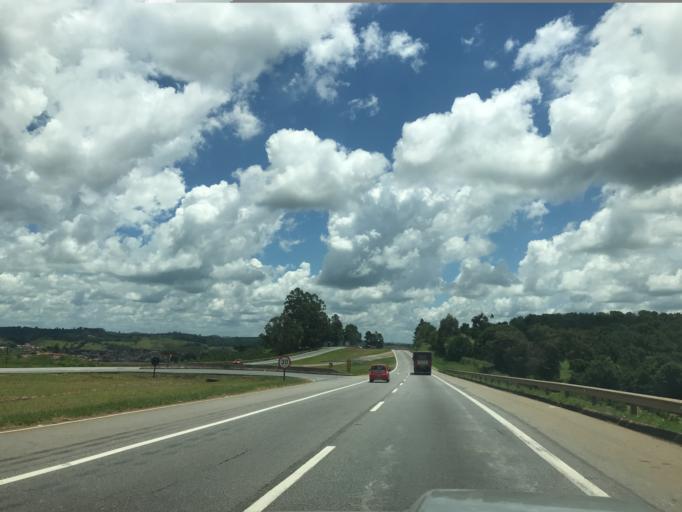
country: BR
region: Minas Gerais
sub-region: Tres Coracoes
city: Tres Coracoes
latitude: -21.4724
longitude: -45.2041
